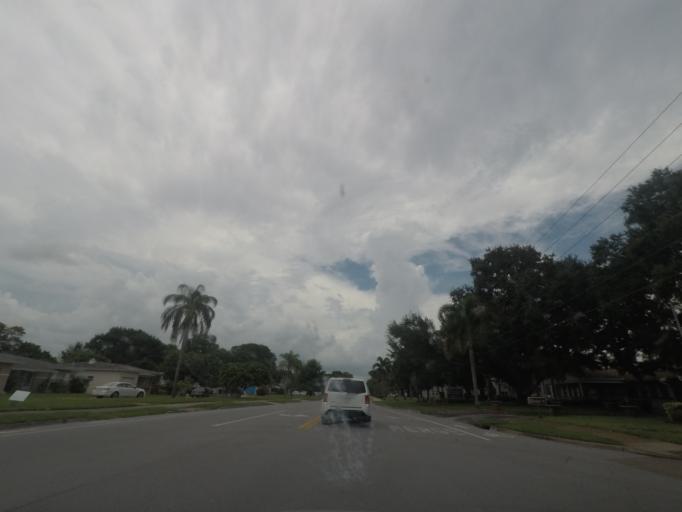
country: US
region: Florida
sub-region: Pinellas County
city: Lealman
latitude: 27.7992
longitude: -82.6775
